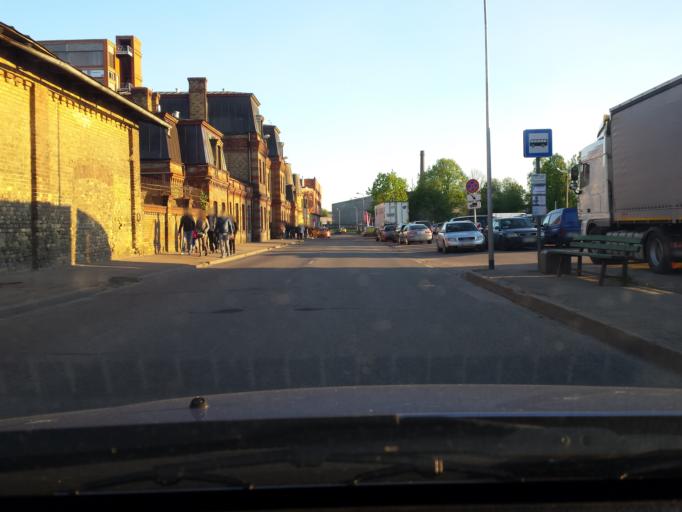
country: LV
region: Riga
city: Riga
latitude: 57.0059
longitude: 24.1202
